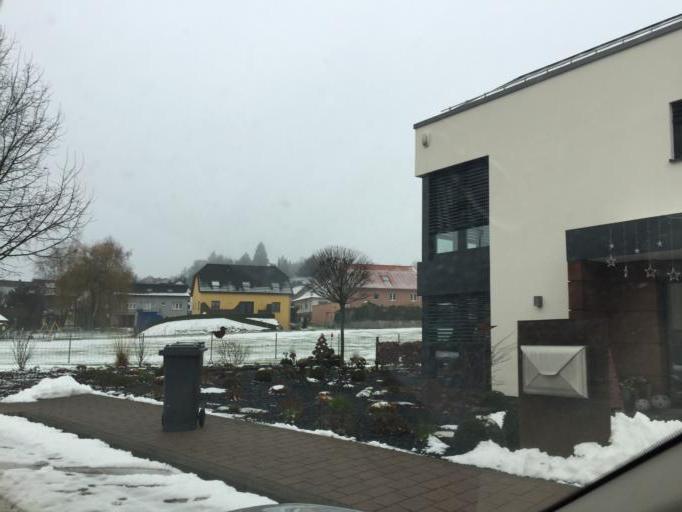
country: LU
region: Diekirch
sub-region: Canton de Diekirch
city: Niederfeulen
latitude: 49.8557
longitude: 6.0507
